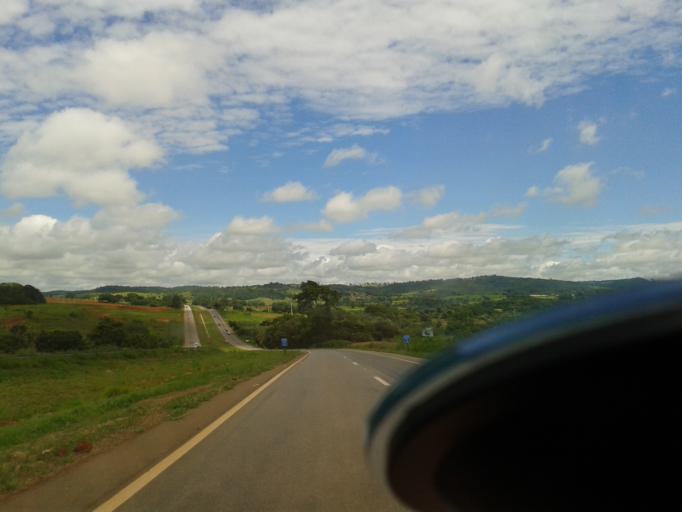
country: BR
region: Goias
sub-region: Inhumas
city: Inhumas
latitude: -16.2316
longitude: -49.5593
